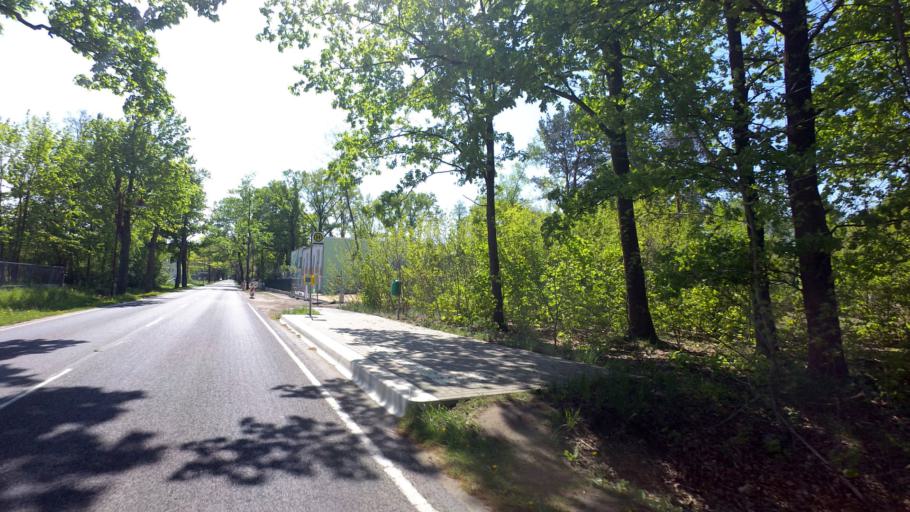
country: DE
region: Brandenburg
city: Bestensee
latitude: 52.2368
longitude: 13.6666
